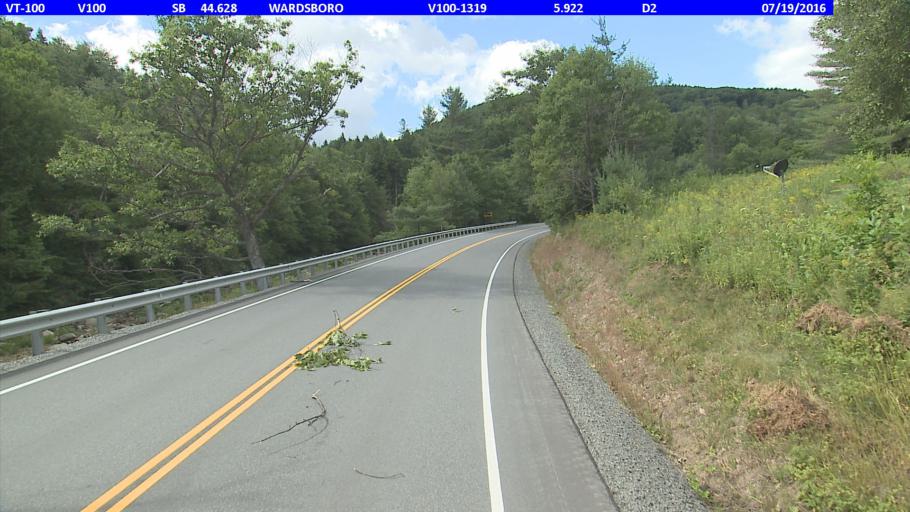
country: US
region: Vermont
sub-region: Windham County
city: Dover
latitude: 43.0840
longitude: -72.8660
